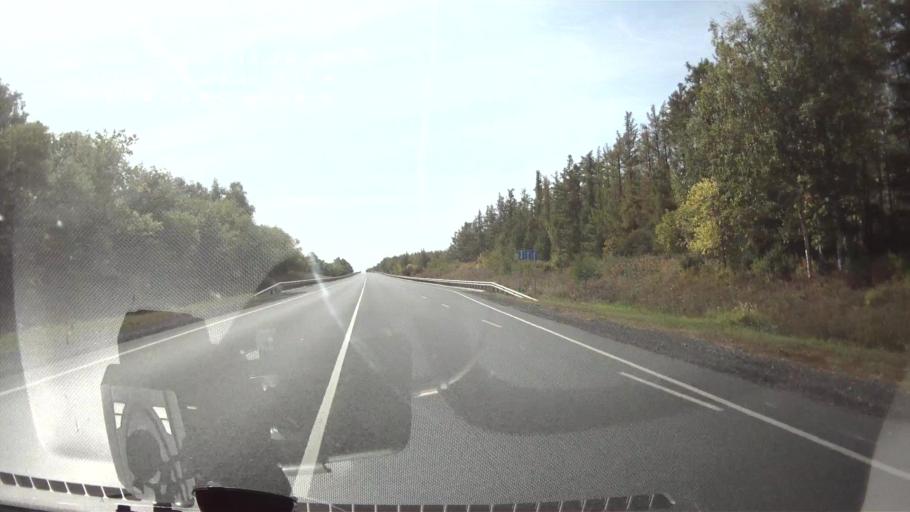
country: RU
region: Saratov
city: Khvalynsk
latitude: 52.5690
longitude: 48.0998
